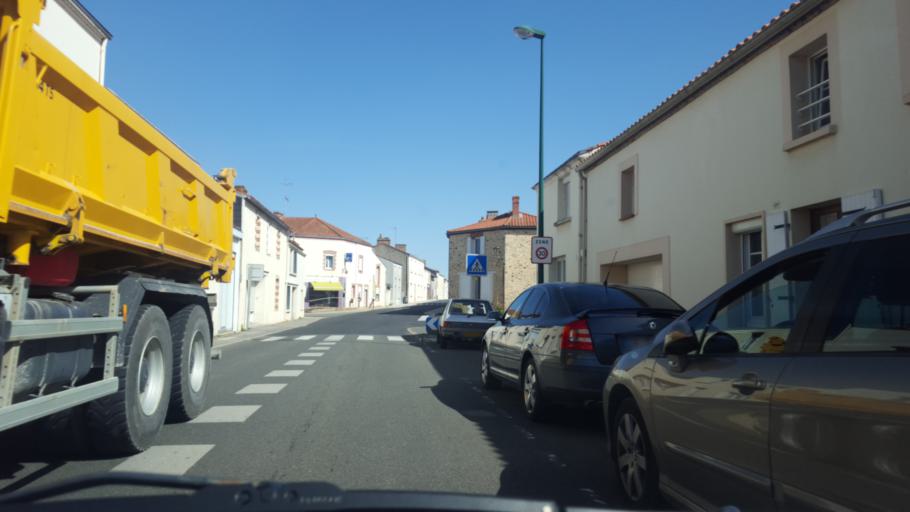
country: FR
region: Pays de la Loire
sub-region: Departement de la Loire-Atlantique
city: La Limouziniere
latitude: 46.9925
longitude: -1.5983
